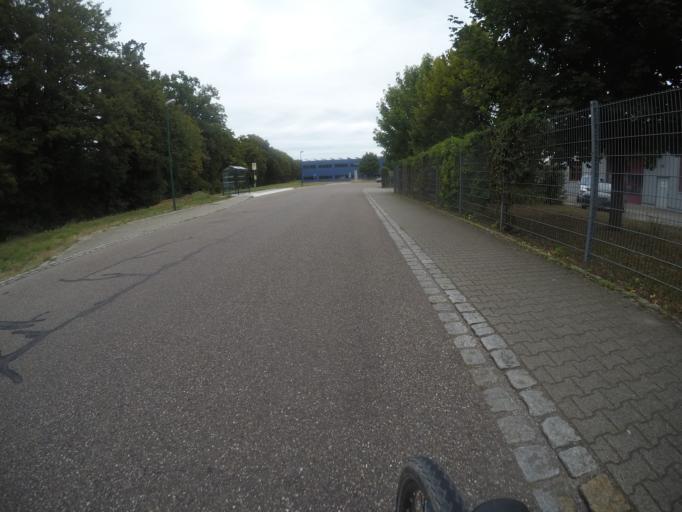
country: DE
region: Baden-Wuerttemberg
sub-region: Karlsruhe Region
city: Muhlacker
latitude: 48.9528
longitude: 8.8784
